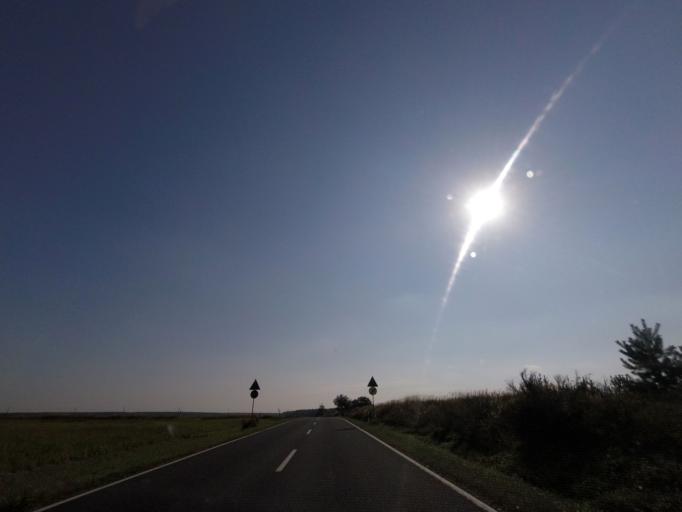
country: DE
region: Brandenburg
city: Niedergorsdorf
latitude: 51.9020
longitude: 13.0243
